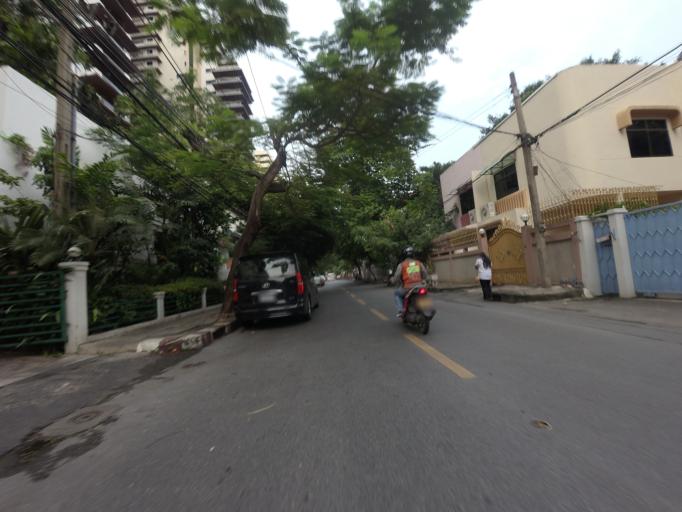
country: TH
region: Bangkok
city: Watthana
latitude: 13.7418
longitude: 100.5635
